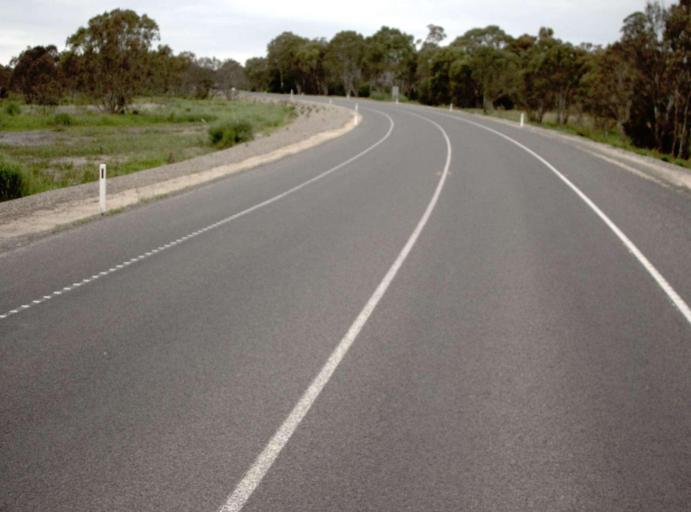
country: AU
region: Victoria
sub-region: Wellington
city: Sale
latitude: -38.1294
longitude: 147.0708
